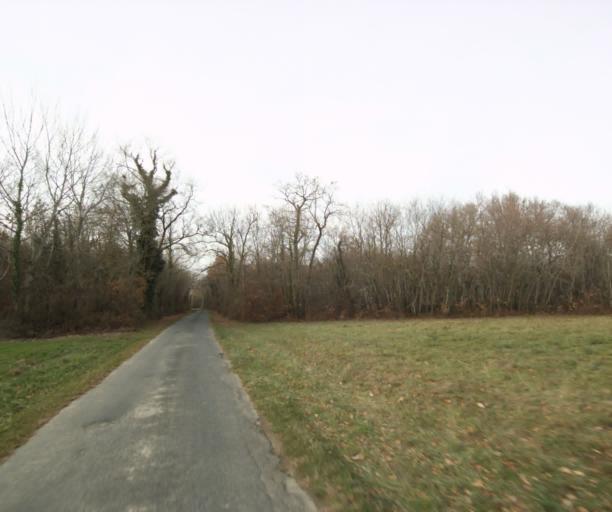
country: FR
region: Poitou-Charentes
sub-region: Departement de la Charente-Maritime
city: Fontcouverte
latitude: 45.7947
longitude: -0.6030
